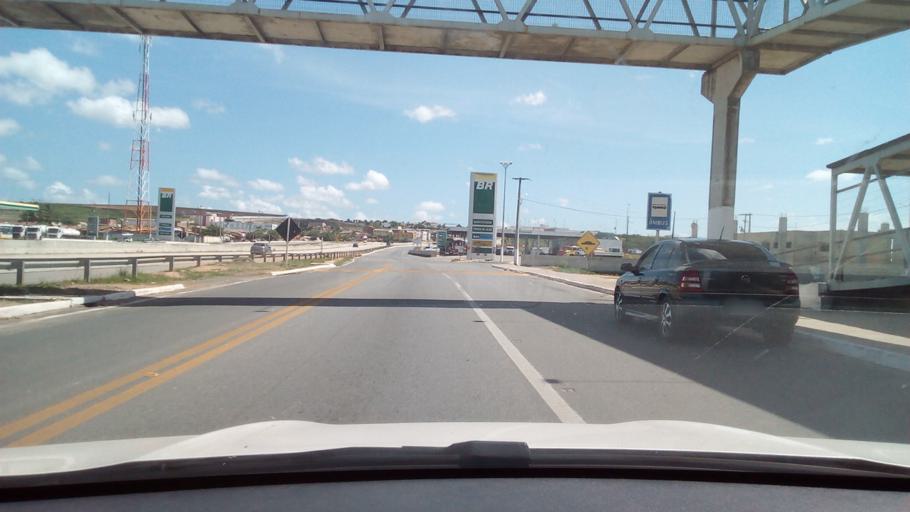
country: BR
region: Rio Grande do Norte
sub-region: Goianinha
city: Goianinha
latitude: -6.2694
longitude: -35.2097
